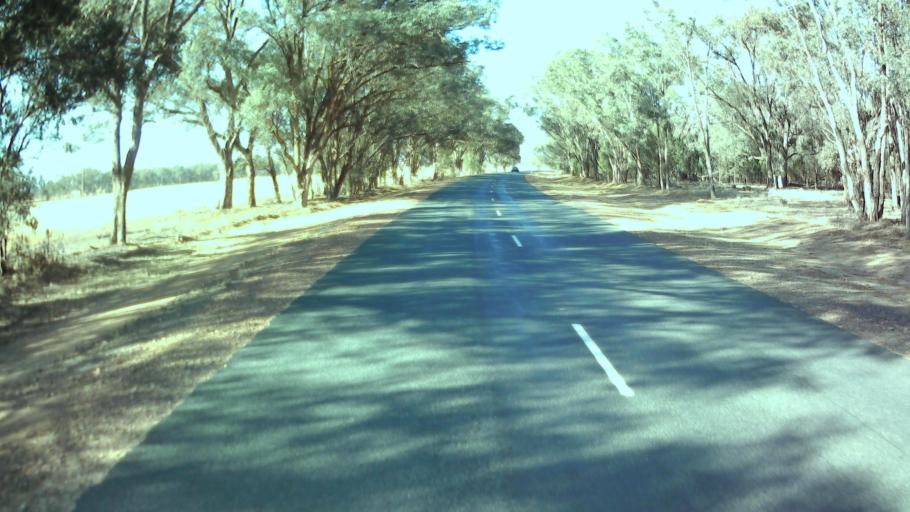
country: AU
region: New South Wales
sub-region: Weddin
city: Grenfell
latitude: -34.0080
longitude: 148.1216
